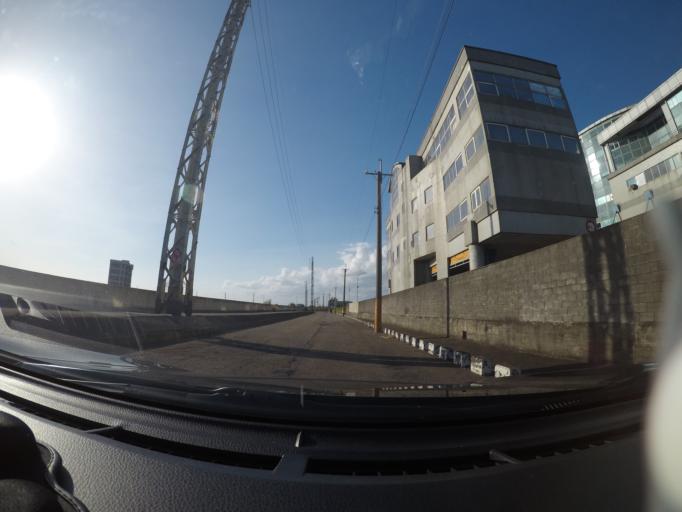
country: TW
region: Taiwan
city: Taoyuan City
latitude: 25.1077
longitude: 121.2500
